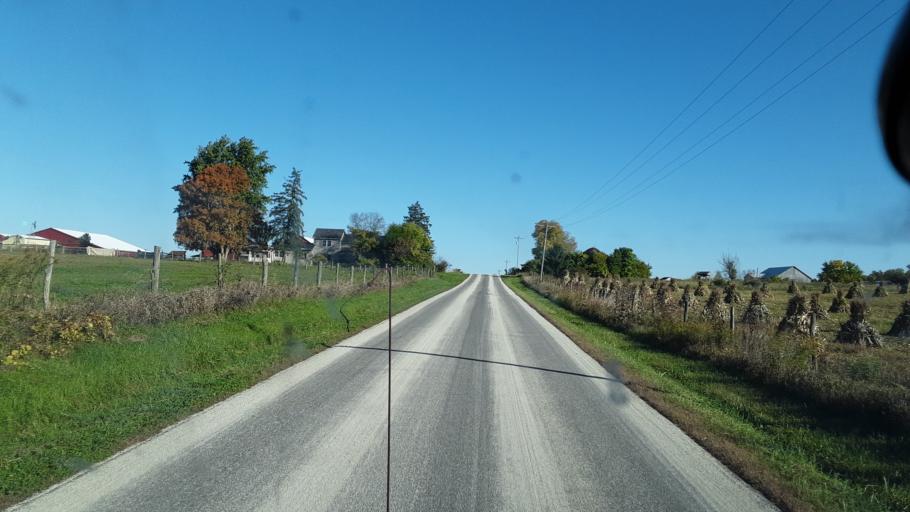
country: US
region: Ohio
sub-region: Hardin County
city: Kenton
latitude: 40.6315
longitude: -83.5381
